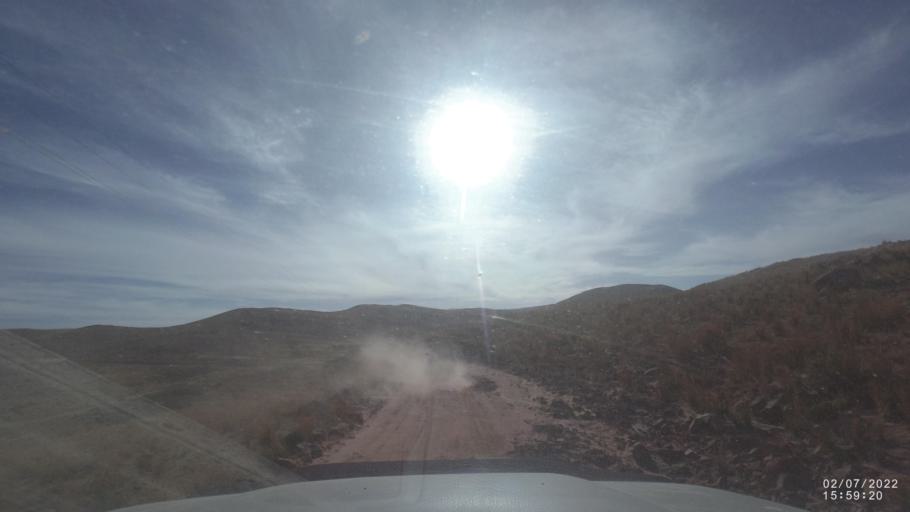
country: BO
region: Cochabamba
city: Irpa Irpa
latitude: -17.9073
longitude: -66.4336
